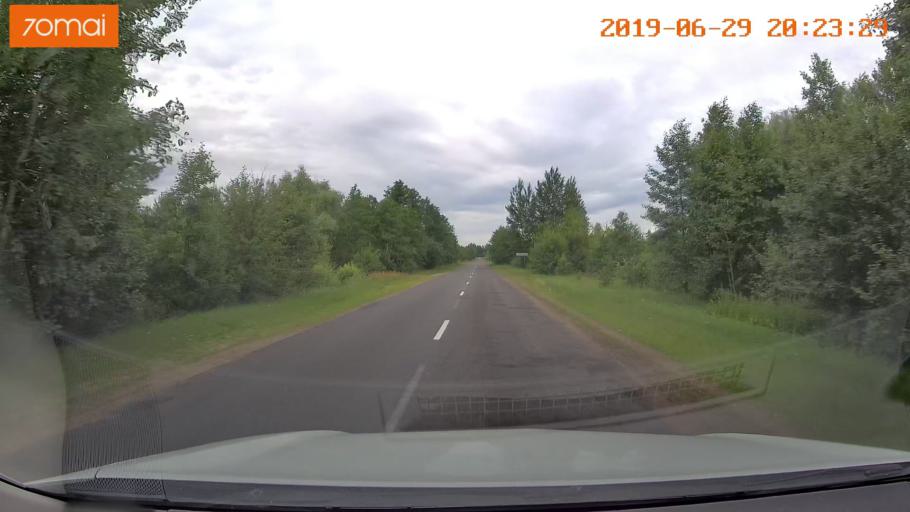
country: BY
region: Brest
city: Asnyezhytsy
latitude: 52.4451
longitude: 26.2609
